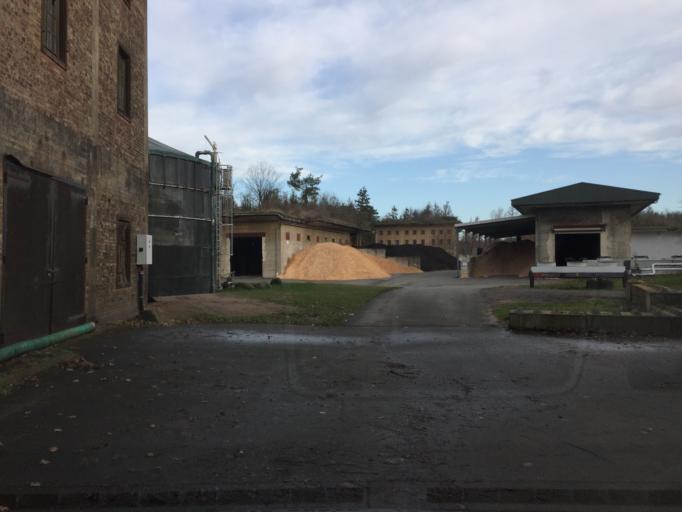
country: DE
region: Lower Saxony
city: Leese
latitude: 52.5231
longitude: 9.1356
